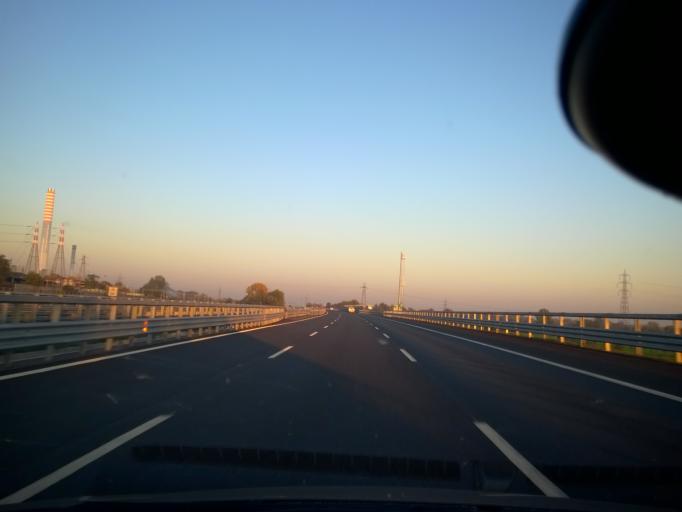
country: IT
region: Lombardy
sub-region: Citta metropolitana di Milano
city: Albignano
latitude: 45.5058
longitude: 9.5000
